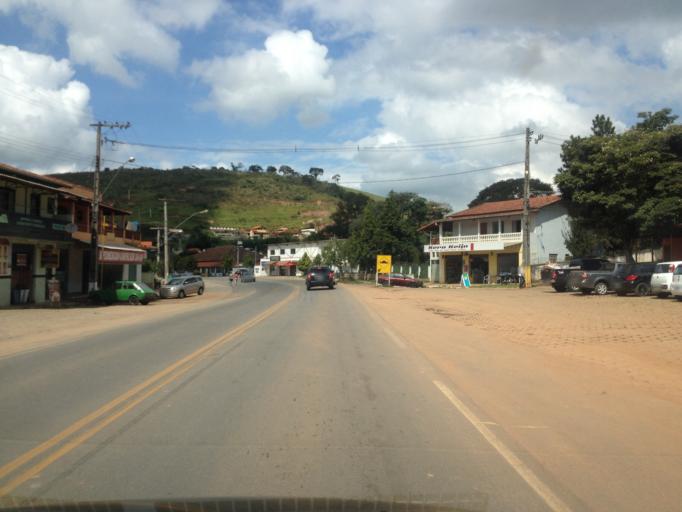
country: BR
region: Minas Gerais
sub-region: Itanhandu
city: Itanhandu
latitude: -22.1952
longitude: -44.9751
